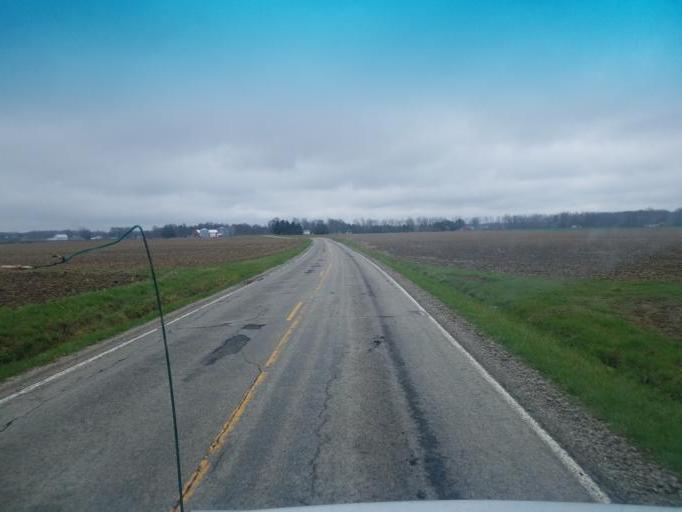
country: US
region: Ohio
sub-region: Richland County
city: Shelby
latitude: 40.9232
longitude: -82.6434
